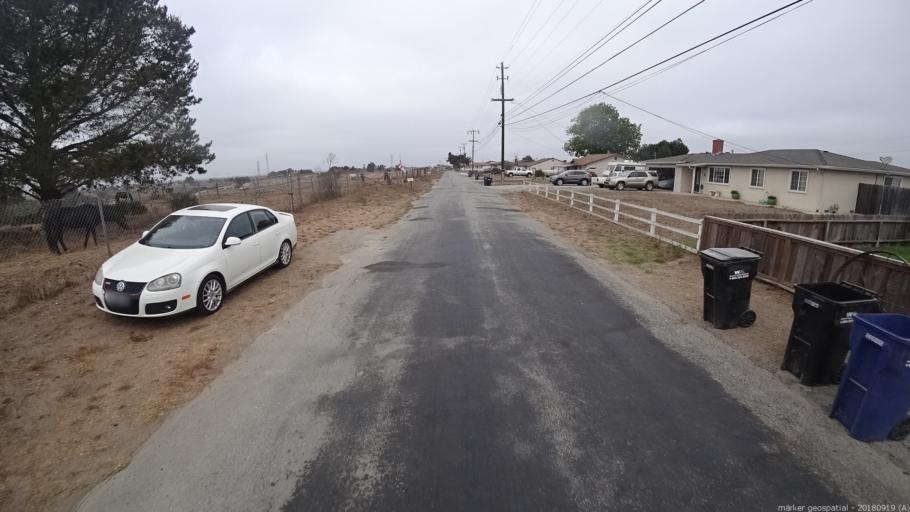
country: US
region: California
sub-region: Monterey County
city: Elkhorn
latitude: 36.7992
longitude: -121.7227
